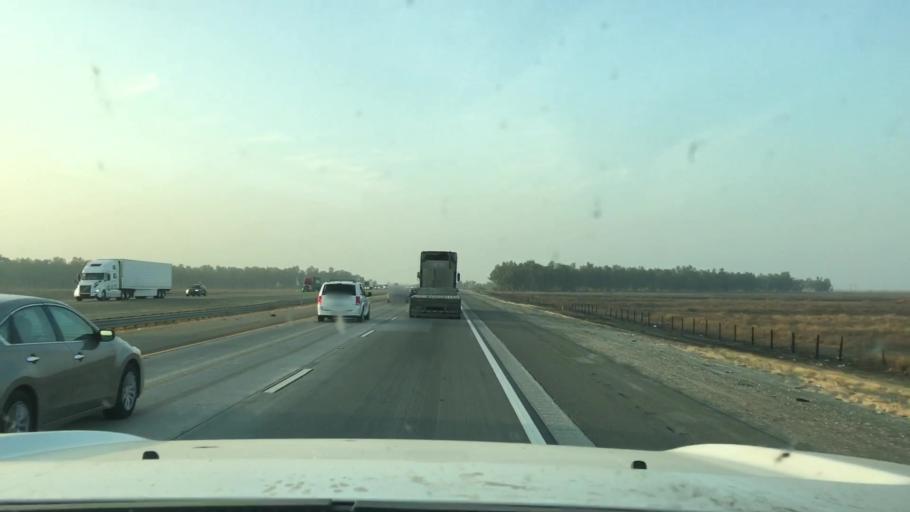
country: US
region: California
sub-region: Kern County
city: Lost Hills
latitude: 35.5905
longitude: -119.6304
